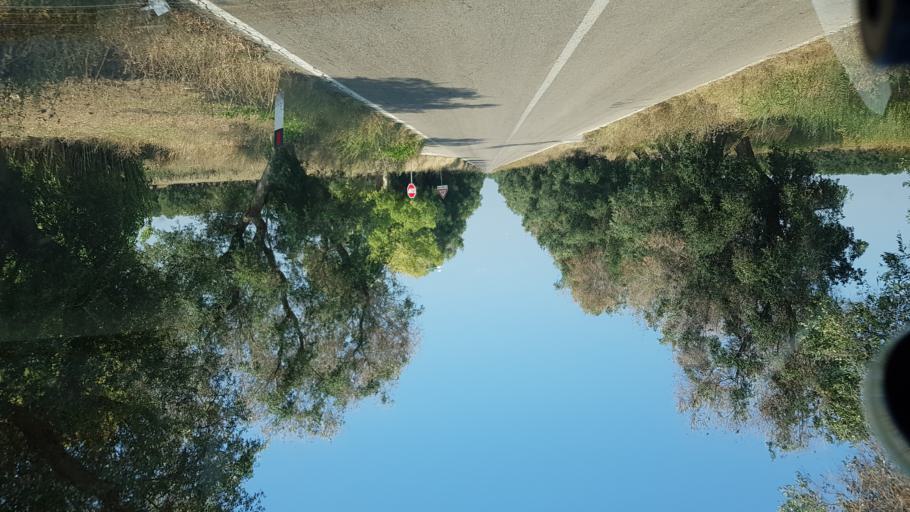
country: IT
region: Apulia
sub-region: Provincia di Brindisi
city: Torre Santa Susanna
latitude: 40.4947
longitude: 17.7066
